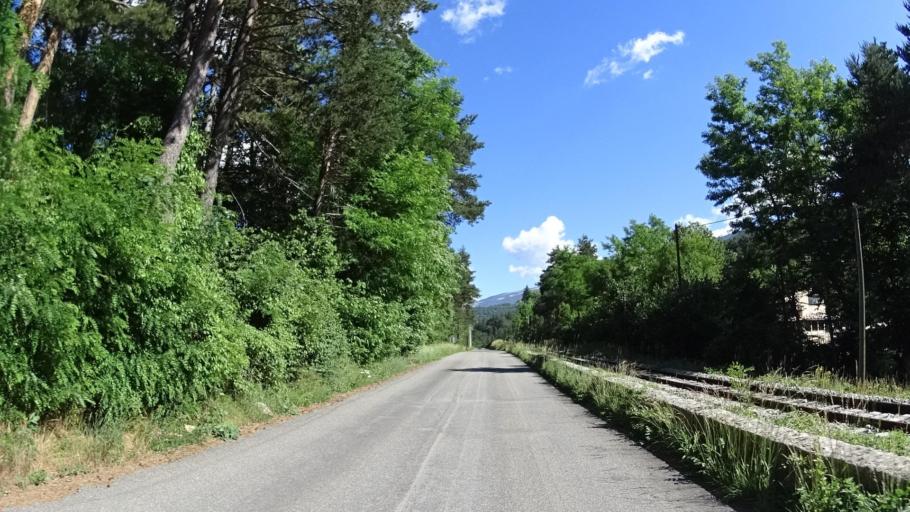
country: FR
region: Provence-Alpes-Cote d'Azur
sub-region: Departement des Alpes-de-Haute-Provence
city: Annot
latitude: 43.9862
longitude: 6.6481
